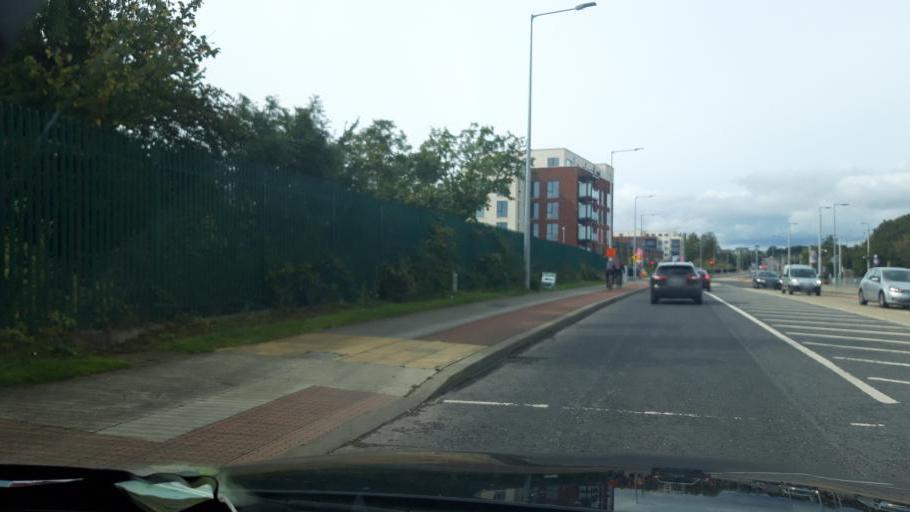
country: IE
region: Leinster
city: Foxrock
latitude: 53.2577
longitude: -6.1972
